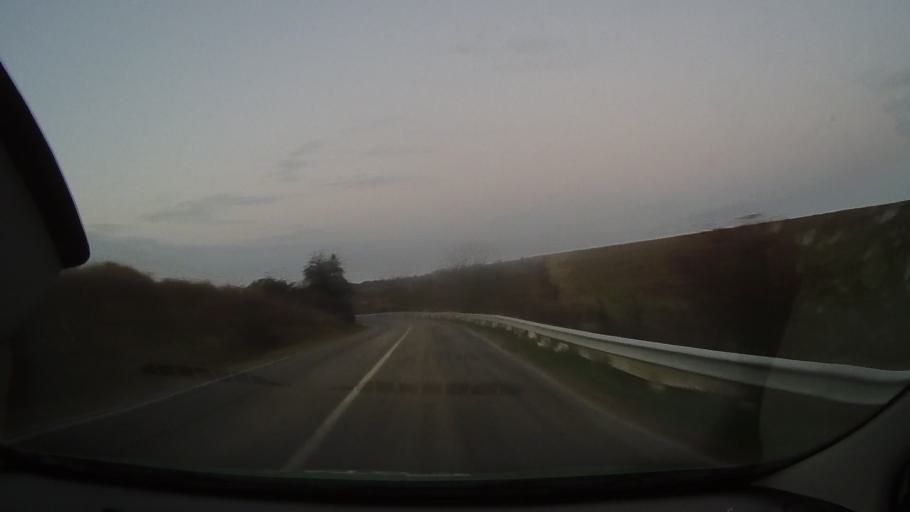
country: RO
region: Constanta
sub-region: Comuna Baneasa
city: Baneasa
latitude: 44.0695
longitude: 27.7353
